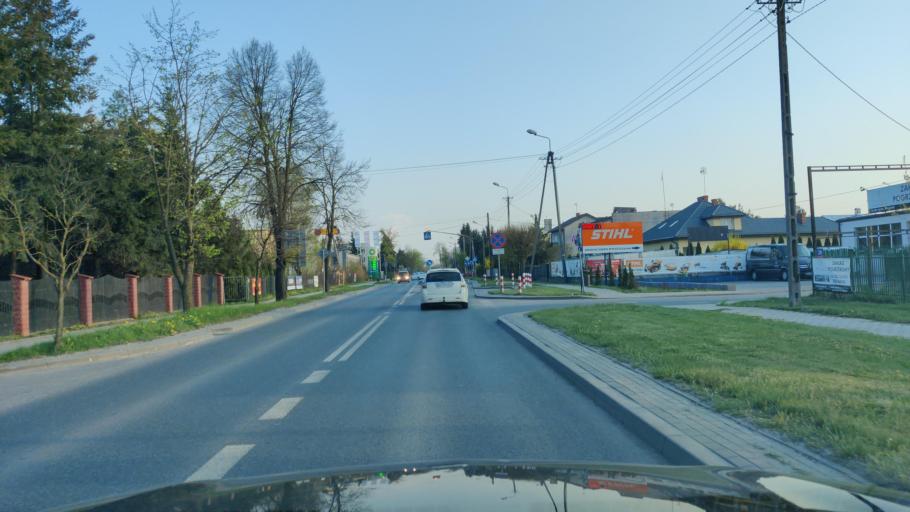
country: PL
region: Masovian Voivodeship
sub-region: Powiat pultuski
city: Pultusk
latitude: 52.6941
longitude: 21.0811
